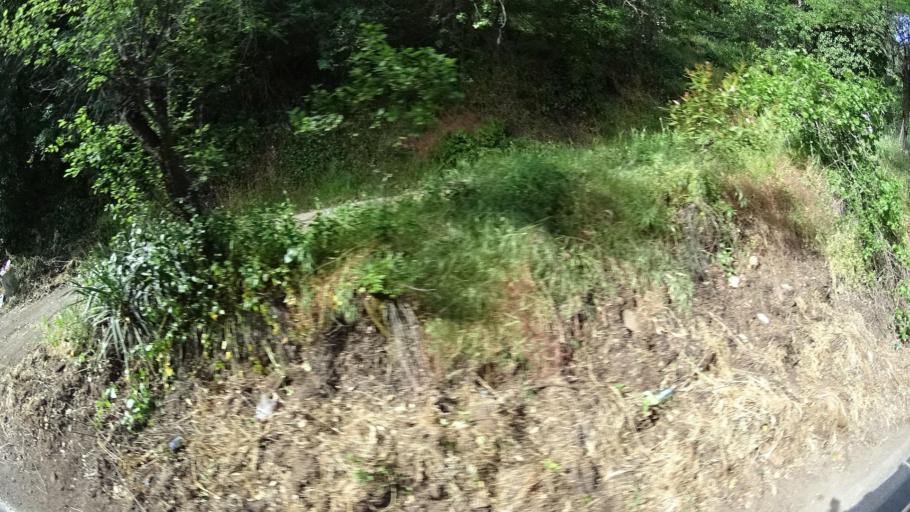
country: US
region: California
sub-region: Lake County
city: Soda Bay
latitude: 39.0015
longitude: -122.7946
